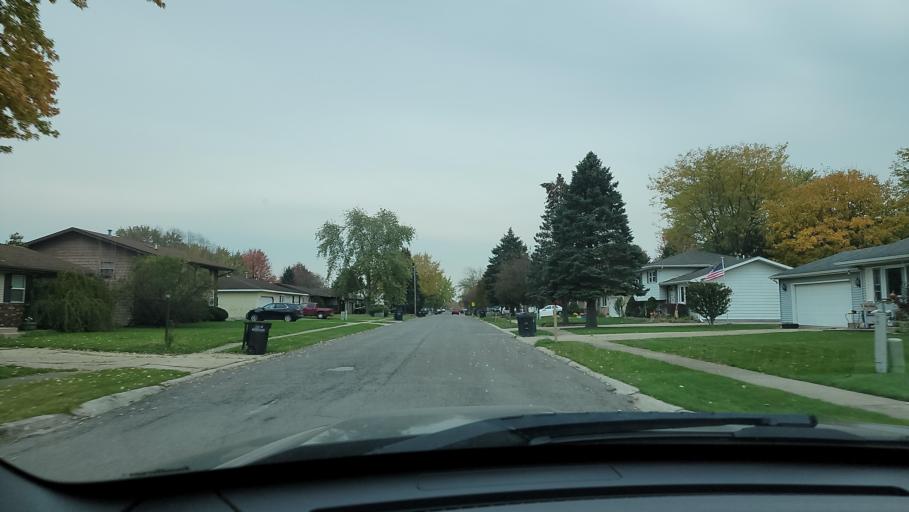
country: US
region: Indiana
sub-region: Lake County
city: Lake Station
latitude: 41.5611
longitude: -87.2138
